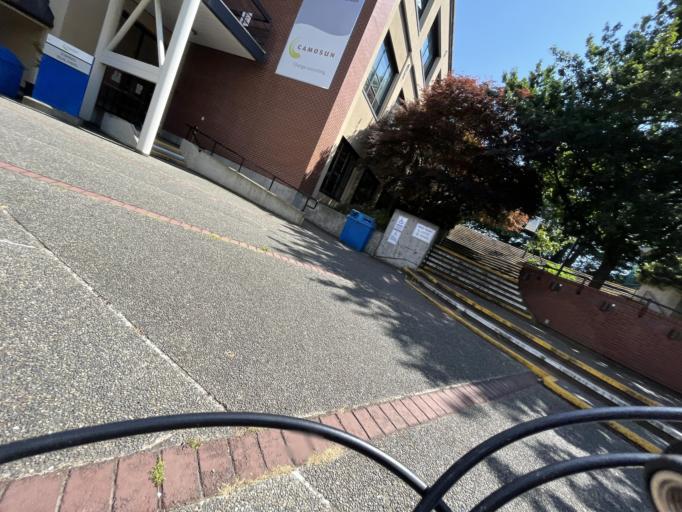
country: CA
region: British Columbia
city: Oak Bay
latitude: 48.4479
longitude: -123.3242
